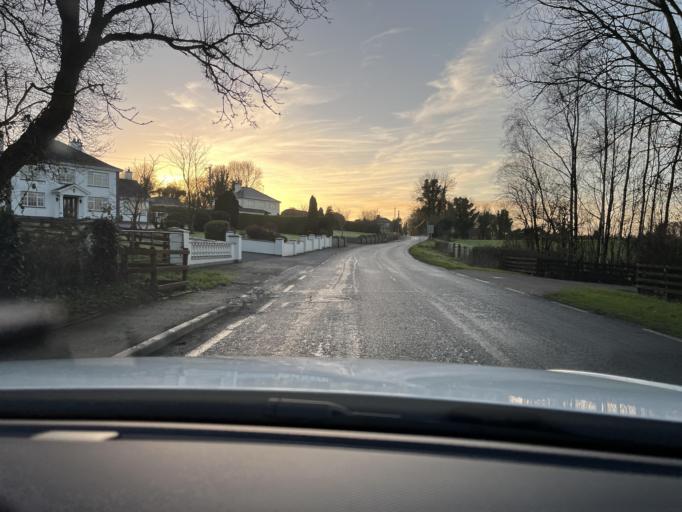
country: IE
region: Ulster
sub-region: An Cabhan
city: Ballyconnell
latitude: 54.0881
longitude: -7.6379
